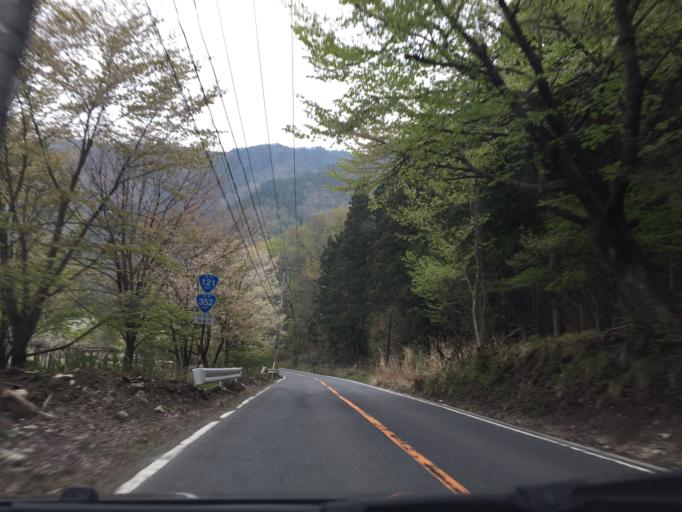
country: JP
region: Tochigi
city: Nikko
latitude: 36.9597
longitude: 139.6976
